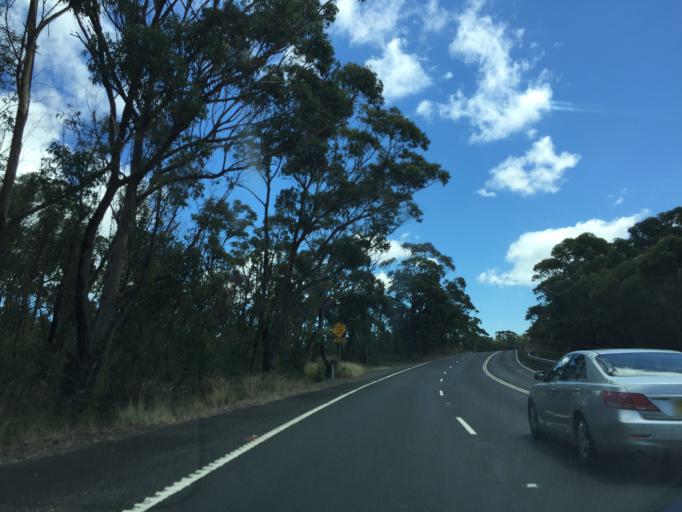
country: AU
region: New South Wales
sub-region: Blue Mountains Municipality
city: Blackheath
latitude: -33.5720
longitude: 150.3577
